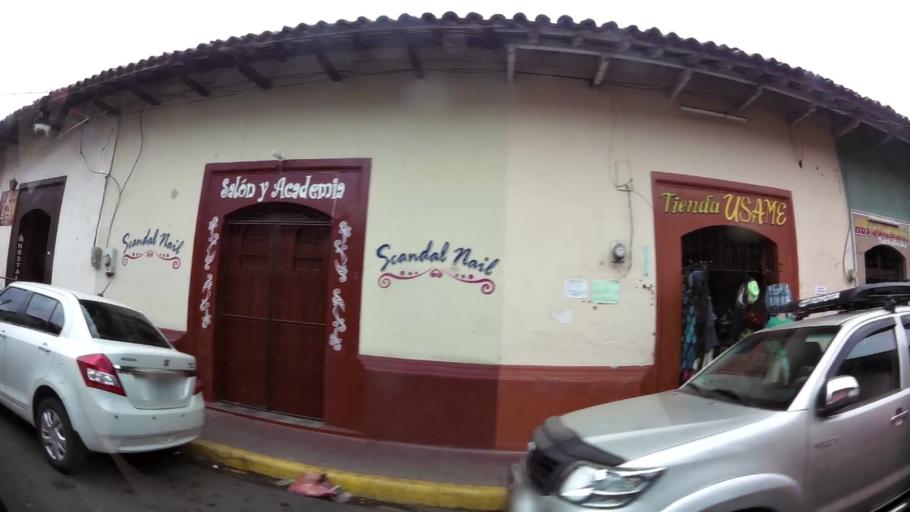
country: NI
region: Leon
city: Leon
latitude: 12.4356
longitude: -86.8751
